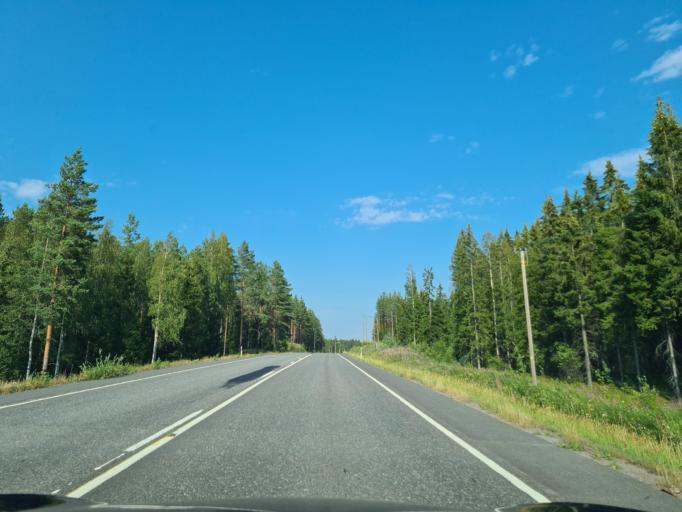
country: FI
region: Satakunta
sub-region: Pohjois-Satakunta
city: Kankaanpaeae
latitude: 61.8288
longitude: 22.3931
